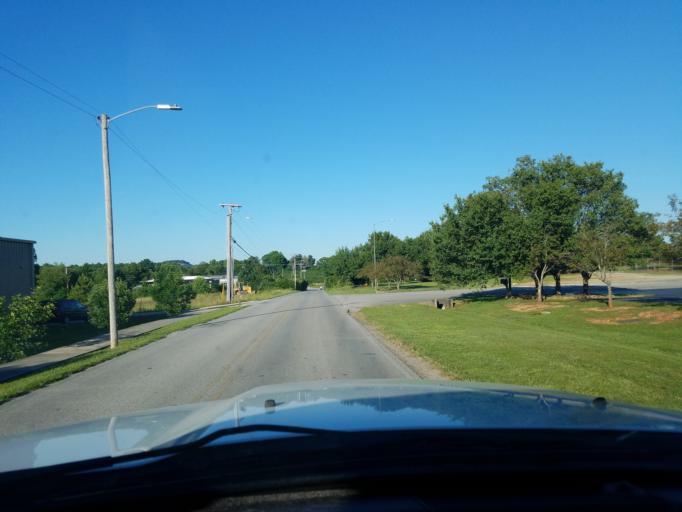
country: US
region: Tennessee
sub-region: Putnam County
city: Cookeville
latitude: 36.1262
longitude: -85.5092
